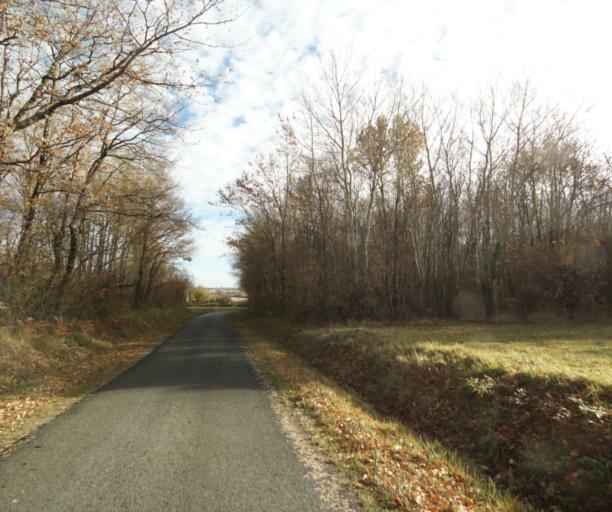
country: FR
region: Poitou-Charentes
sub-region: Departement de la Charente-Maritime
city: Corme-Royal
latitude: 45.7272
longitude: -0.7735
